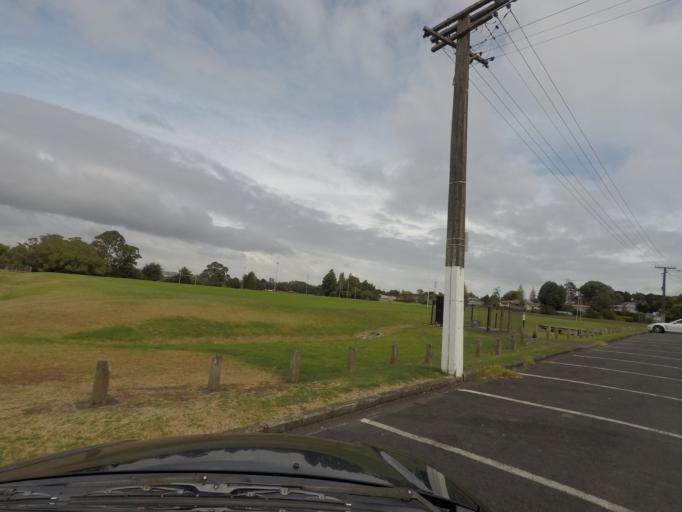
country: NZ
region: Auckland
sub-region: Auckland
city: Rosebank
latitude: -36.8939
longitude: 174.6699
